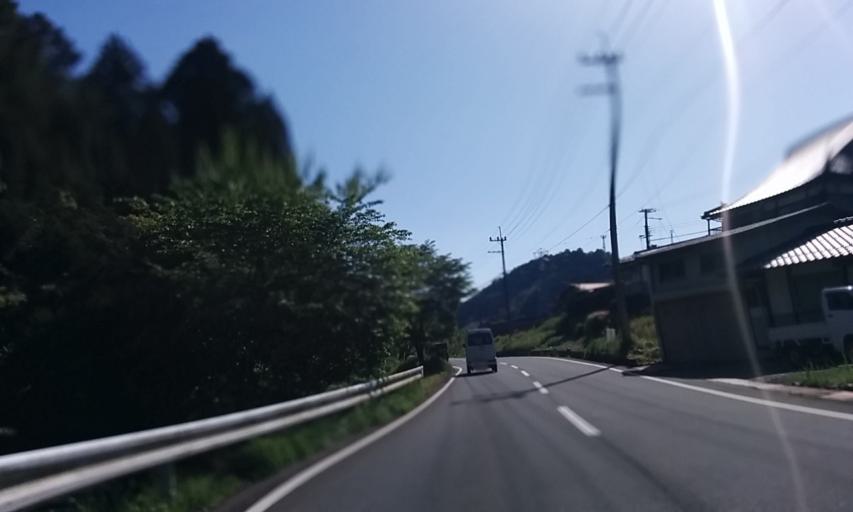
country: JP
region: Kyoto
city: Ayabe
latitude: 35.2579
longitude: 135.4271
